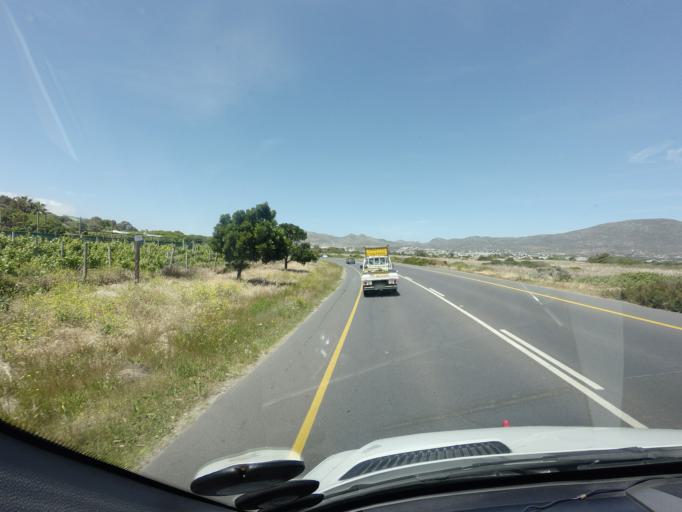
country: ZA
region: Western Cape
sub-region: City of Cape Town
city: Constantia
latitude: -34.1127
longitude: 18.3819
